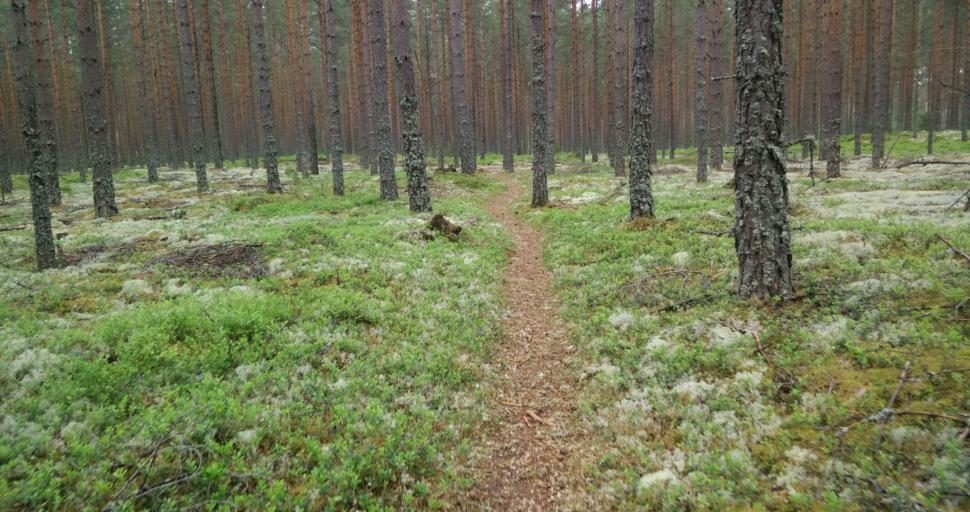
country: SE
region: Vaermland
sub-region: Hagfors Kommun
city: Hagfors
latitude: 60.0149
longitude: 13.5874
